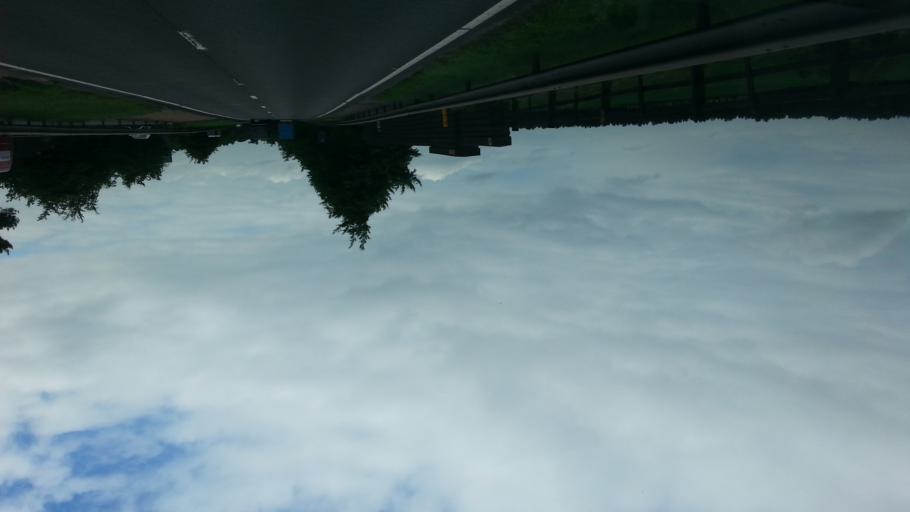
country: GB
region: England
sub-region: Nottinghamshire
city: Babworth
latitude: 53.3027
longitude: -1.0319
